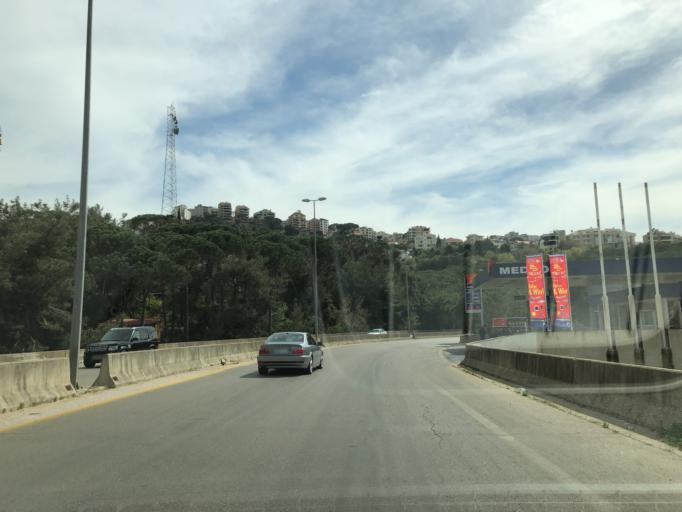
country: LB
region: Mont-Liban
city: Jdaidet el Matn
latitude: 33.8951
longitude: 35.6324
